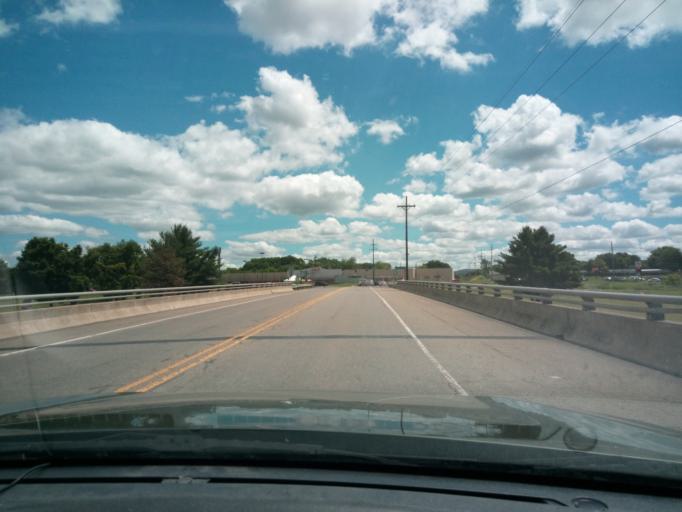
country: US
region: Pennsylvania
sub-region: Bradford County
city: South Waverly
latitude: 41.9890
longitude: -76.5492
